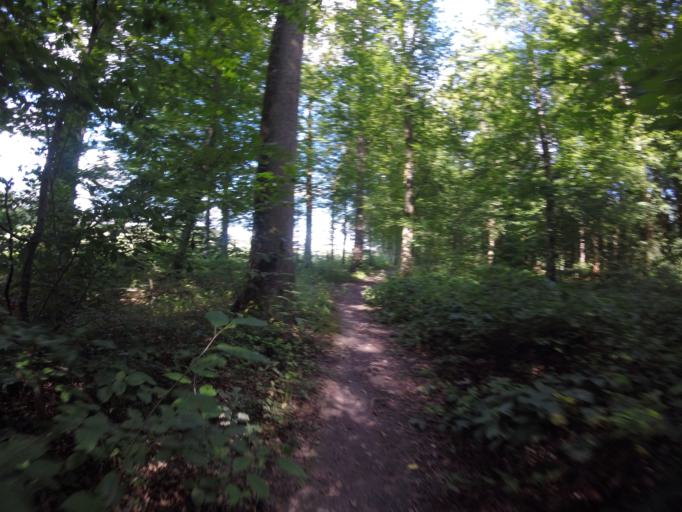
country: DE
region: Baden-Wuerttemberg
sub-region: Regierungsbezirk Stuttgart
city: Backnang
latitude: 48.9619
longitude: 9.4411
